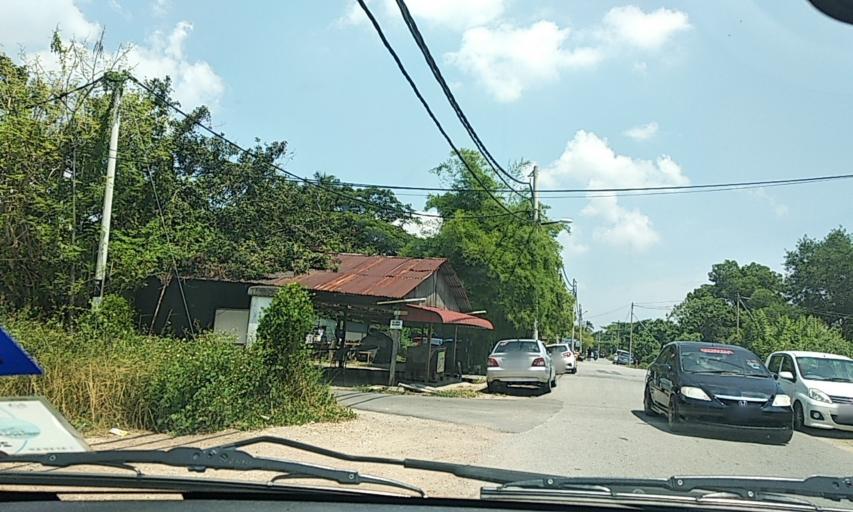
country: MY
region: Kedah
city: Sungai Petani
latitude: 5.6213
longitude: 100.4678
